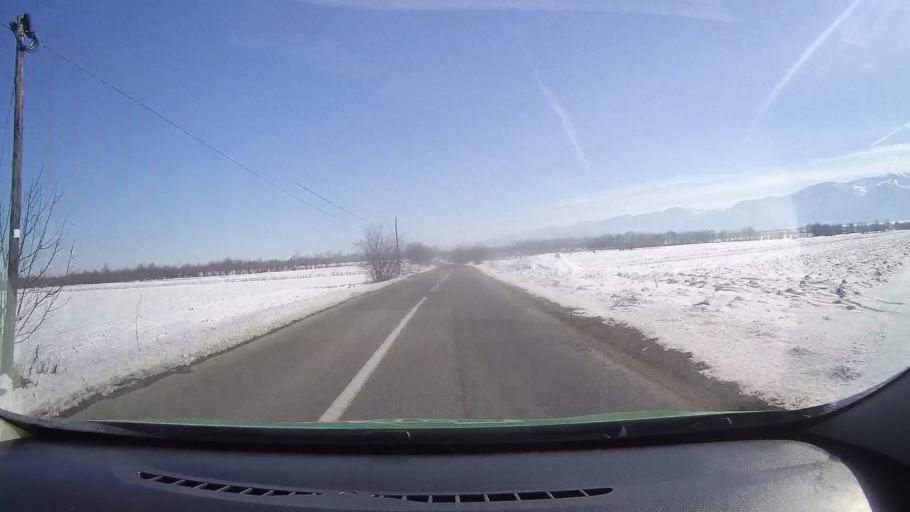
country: RO
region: Brasov
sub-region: Comuna Recea
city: Recea
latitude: 45.7317
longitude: 24.9540
